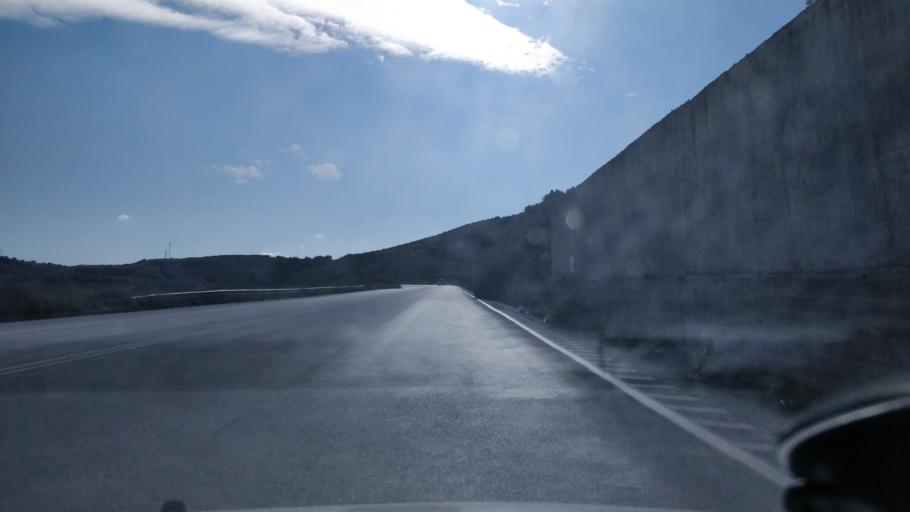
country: GR
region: Crete
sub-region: Nomos Irakleiou
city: Ano Arhanes
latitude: 35.2519
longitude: 25.1779
